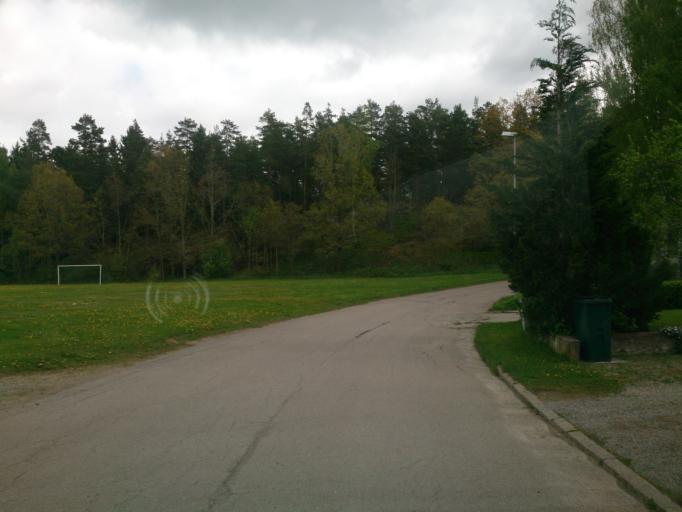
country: SE
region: OEstergoetland
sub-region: Atvidabergs Kommun
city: Atvidaberg
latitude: 58.2123
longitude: 16.0061
